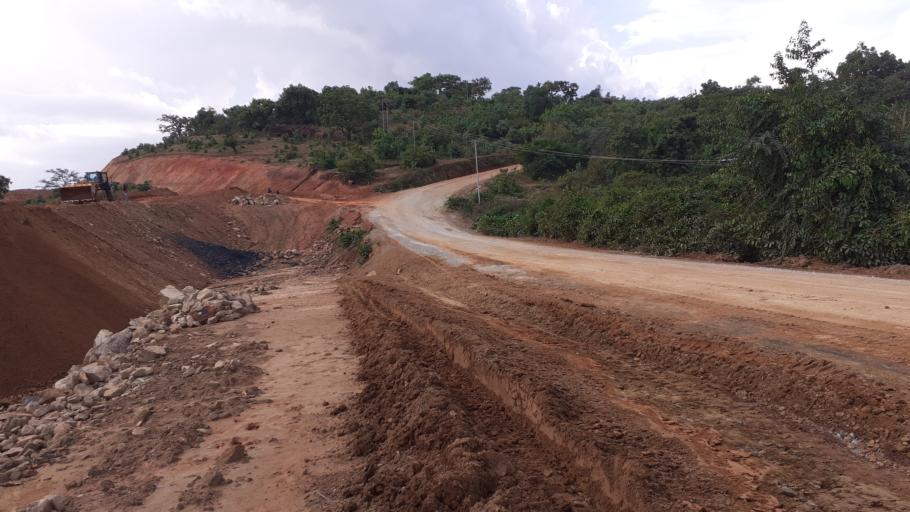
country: ET
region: Oromiya
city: Gimbi
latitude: 9.3205
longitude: 35.6926
